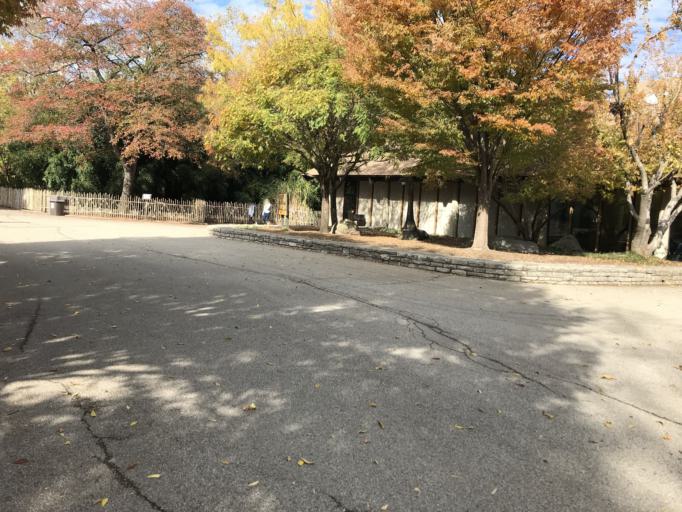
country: US
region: Kentucky
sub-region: Jefferson County
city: Audubon Park
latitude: 38.2058
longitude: -85.7053
